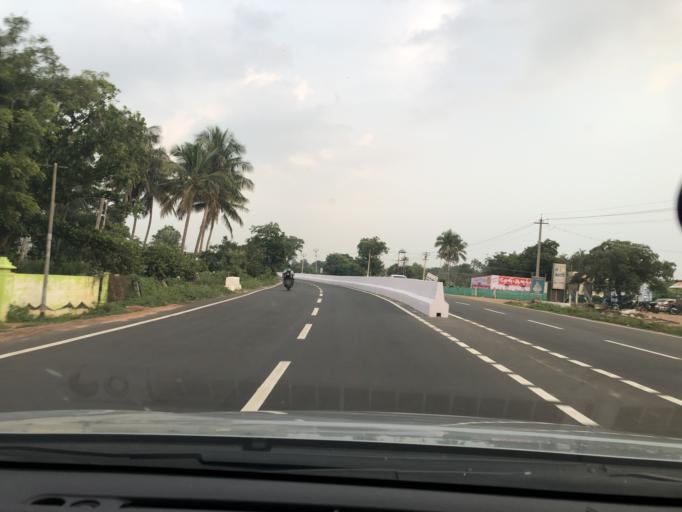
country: IN
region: Tamil Nadu
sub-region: Dindigul
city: Vedasandur
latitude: 10.4660
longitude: 77.8057
